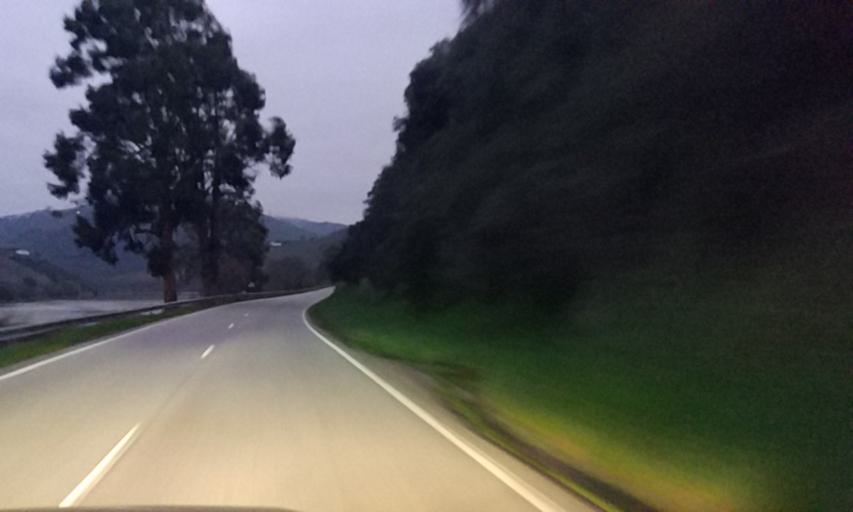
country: PT
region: Viseu
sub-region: Tabuaco
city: Tabuaco
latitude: 41.1577
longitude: -7.6113
